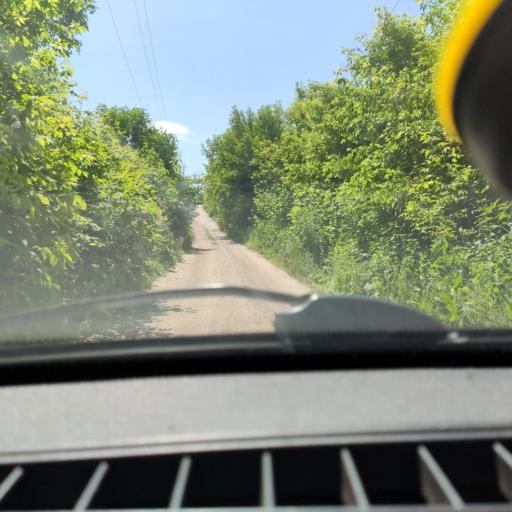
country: RU
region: Samara
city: Zhigulevsk
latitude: 53.3760
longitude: 49.5092
